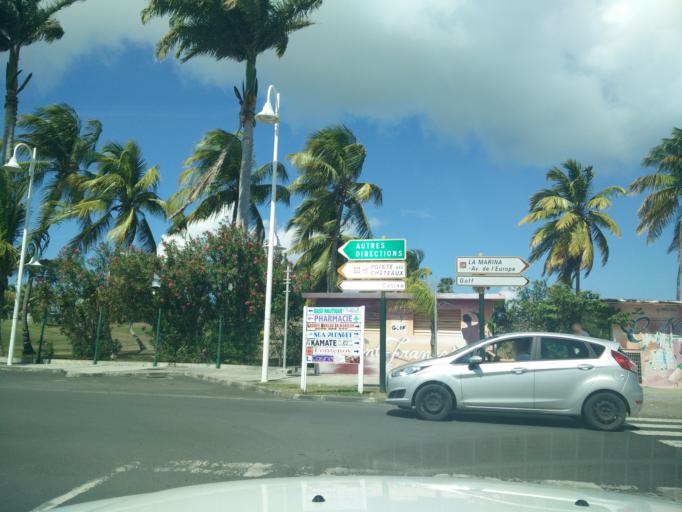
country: GP
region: Guadeloupe
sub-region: Guadeloupe
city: Saint-Francois
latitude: 16.2544
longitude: -61.2699
